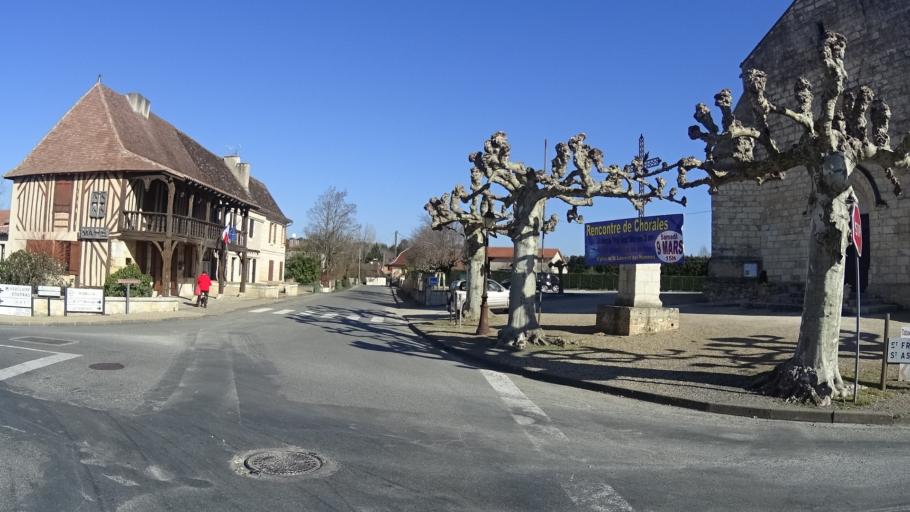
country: FR
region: Aquitaine
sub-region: Departement de la Dordogne
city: Montpon-Menesterol
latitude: 45.0369
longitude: 0.2538
